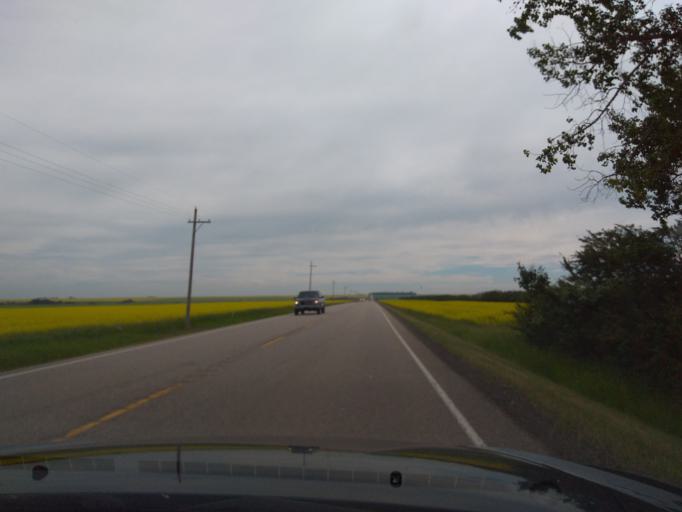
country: CA
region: Alberta
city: Carstairs
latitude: 51.5618
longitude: -113.9826
